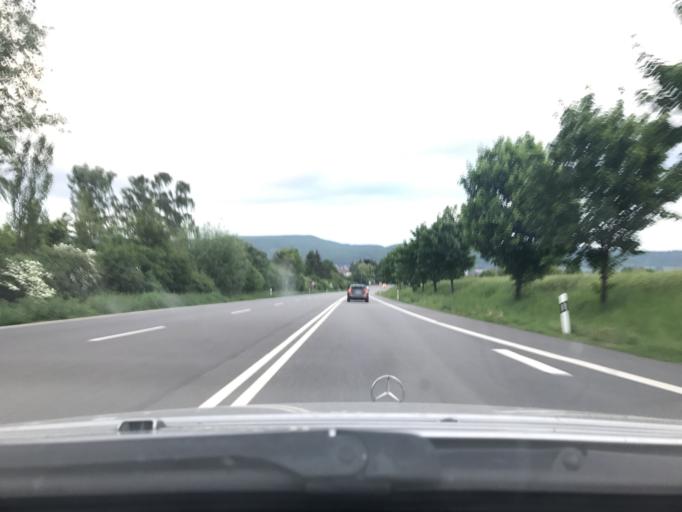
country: DE
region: Hesse
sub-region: Regierungsbezirk Kassel
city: Eschwege
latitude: 51.1792
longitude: 10.0364
